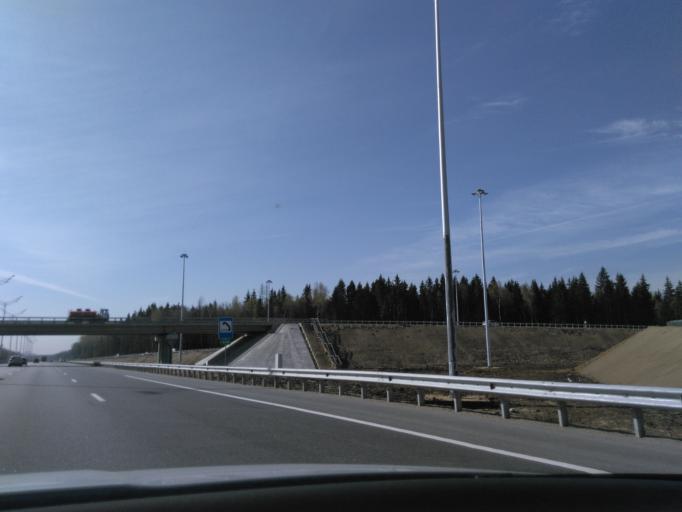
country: RU
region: Moskovskaya
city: Rzhavki
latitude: 56.0088
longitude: 37.2876
